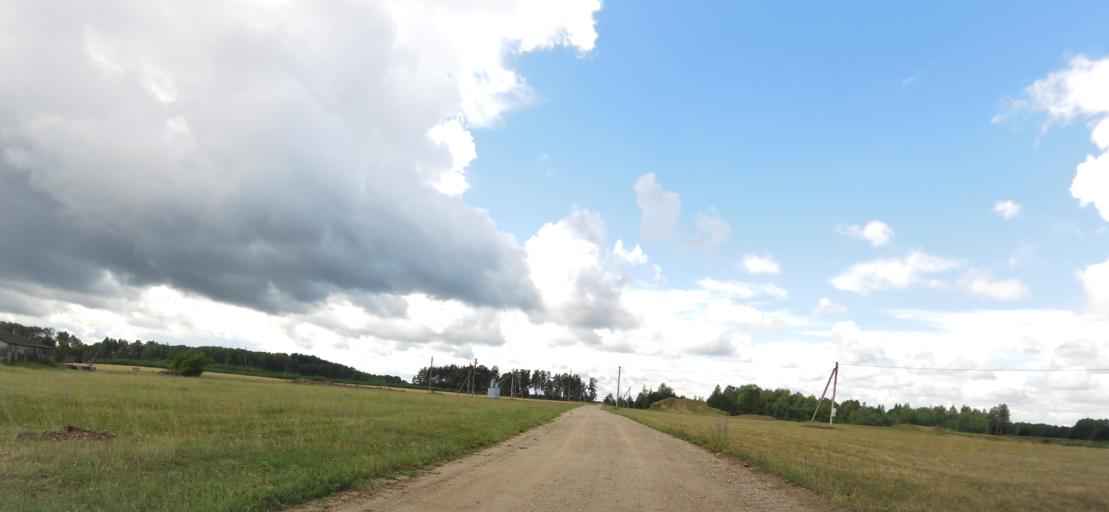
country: LT
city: Vabalninkas
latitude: 55.8872
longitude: 24.7758
